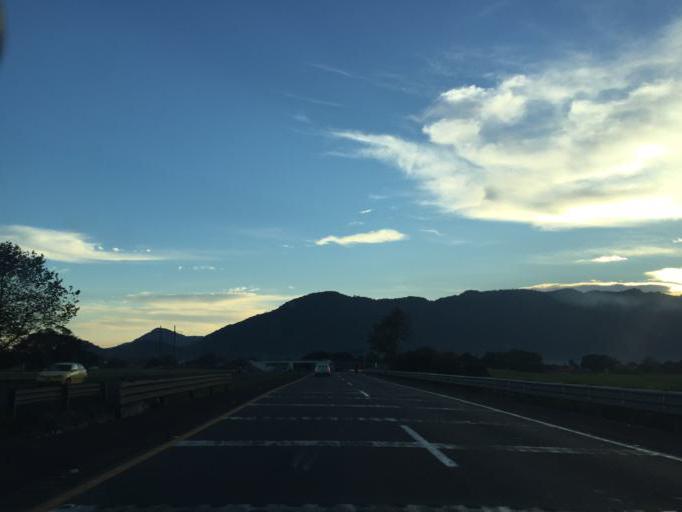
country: MX
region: Veracruz
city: Jalapilla
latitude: 18.8310
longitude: -97.0945
